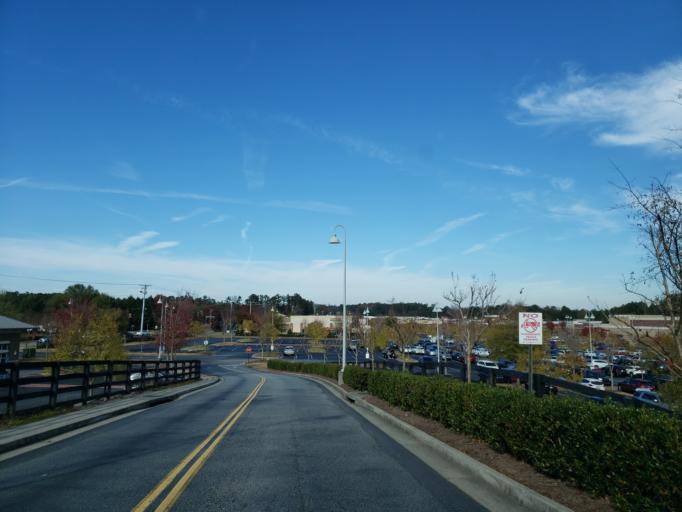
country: US
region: Georgia
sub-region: Fulton County
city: Alpharetta
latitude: 34.0982
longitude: -84.2704
